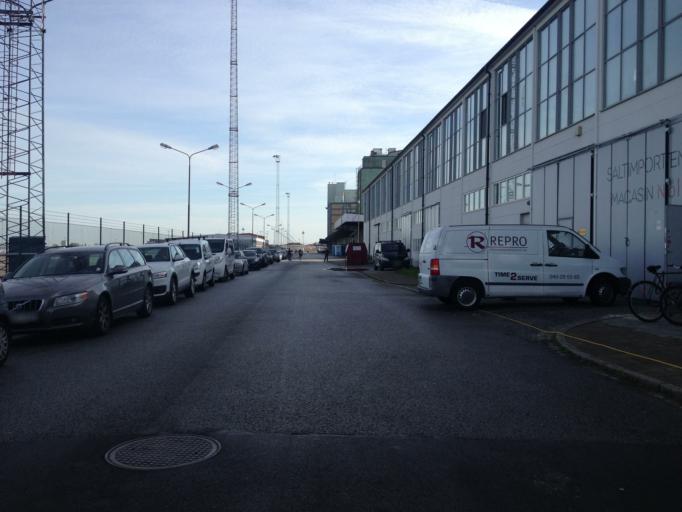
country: SE
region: Skane
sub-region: Malmo
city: Malmoe
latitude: 55.6165
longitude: 12.9972
